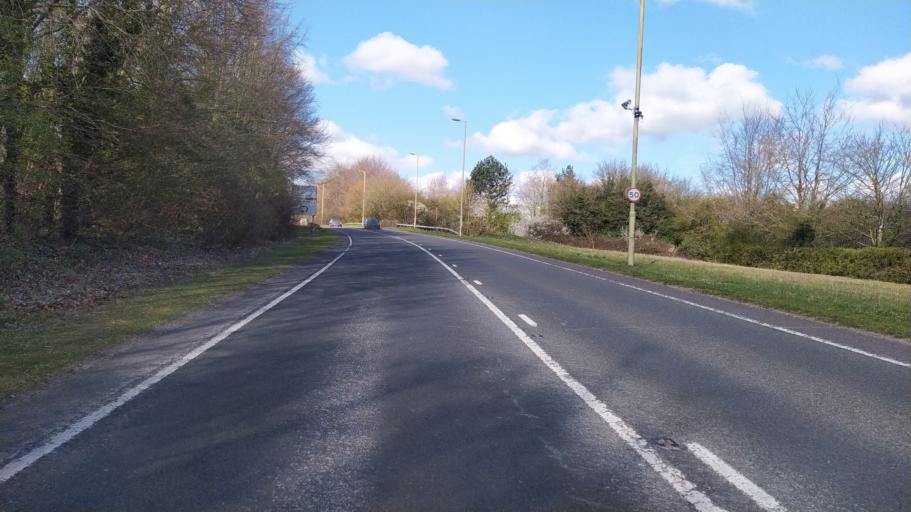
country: GB
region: England
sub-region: Hampshire
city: Andover
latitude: 51.2177
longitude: -1.5045
